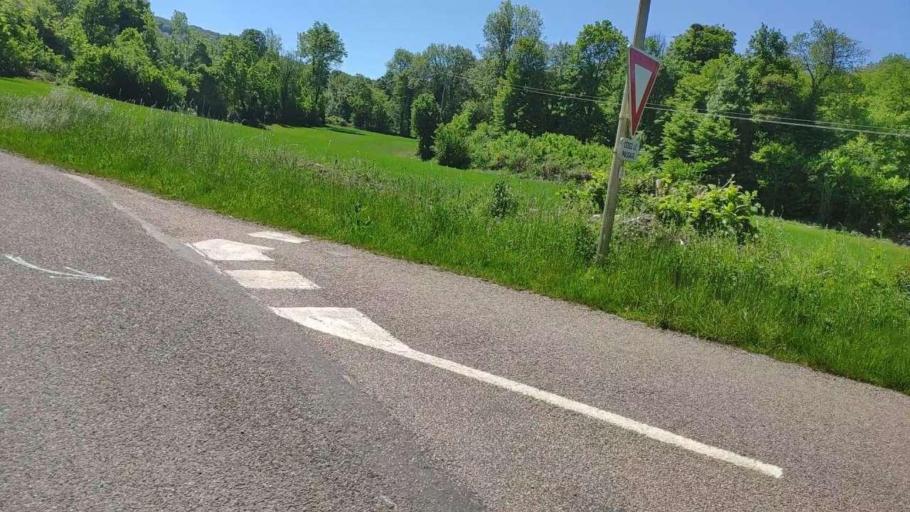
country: FR
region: Franche-Comte
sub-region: Departement du Jura
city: Poligny
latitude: 46.7308
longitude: 5.7405
